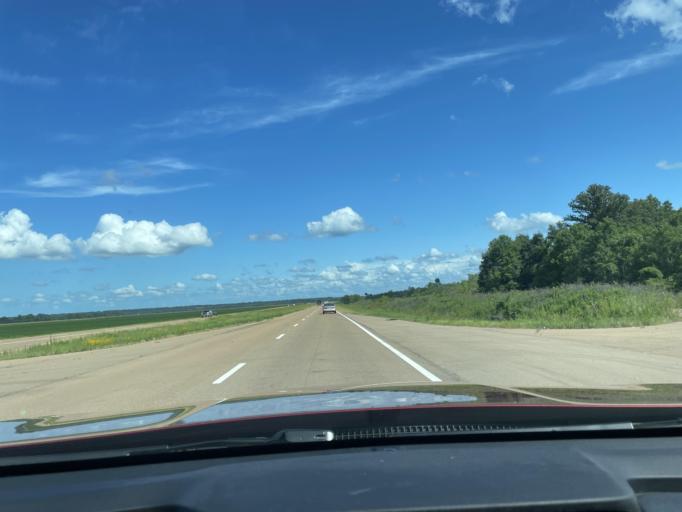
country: US
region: Mississippi
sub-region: Yazoo County
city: Yazoo City
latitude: 32.9563
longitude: -90.4287
